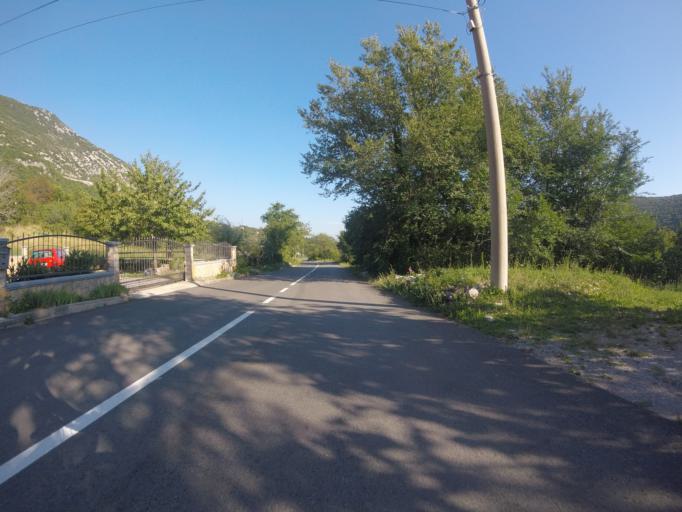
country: HR
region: Primorsko-Goranska
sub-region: Grad Crikvenica
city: Jadranovo
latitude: 45.2541
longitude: 14.6224
